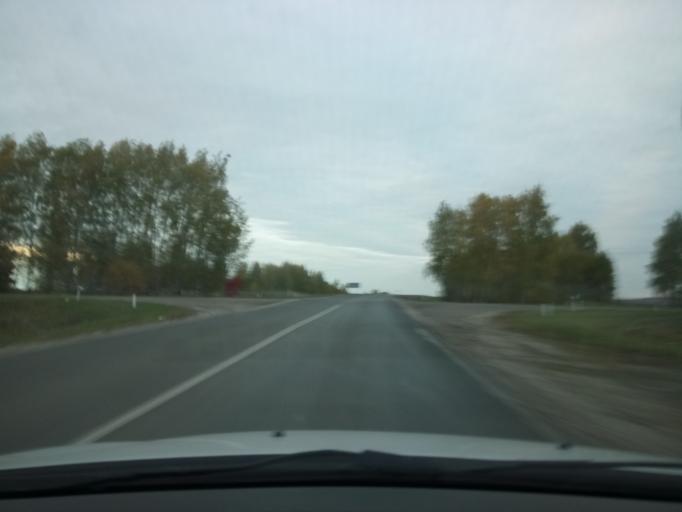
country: RU
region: Nizjnij Novgorod
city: Bol'shoye Murashkino
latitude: 55.7726
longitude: 44.7458
